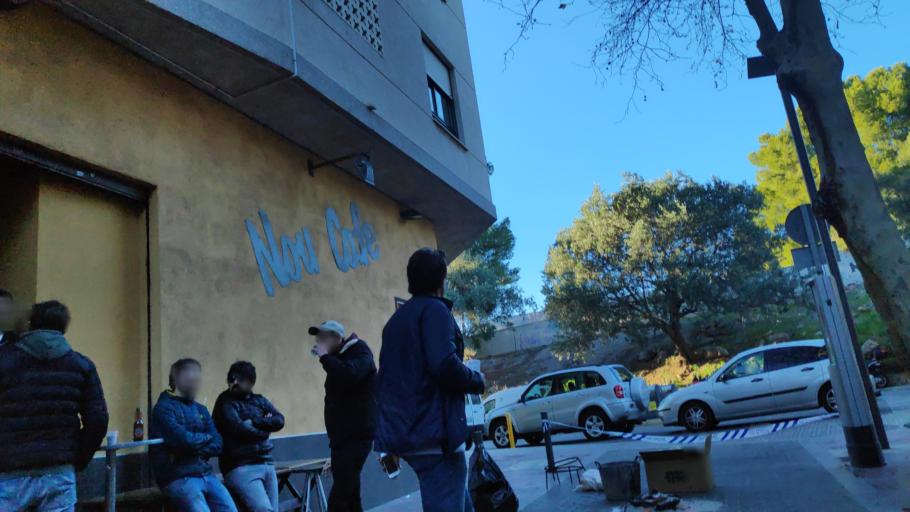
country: ES
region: Valencia
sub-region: Provincia de Castello
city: Benicassim
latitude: 40.0556
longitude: 0.0623
